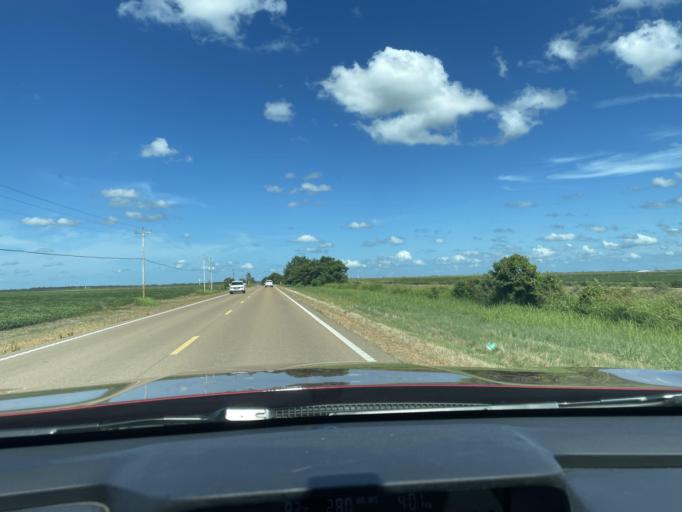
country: US
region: Mississippi
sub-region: Humphreys County
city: Belzoni
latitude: 33.1837
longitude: -90.5424
